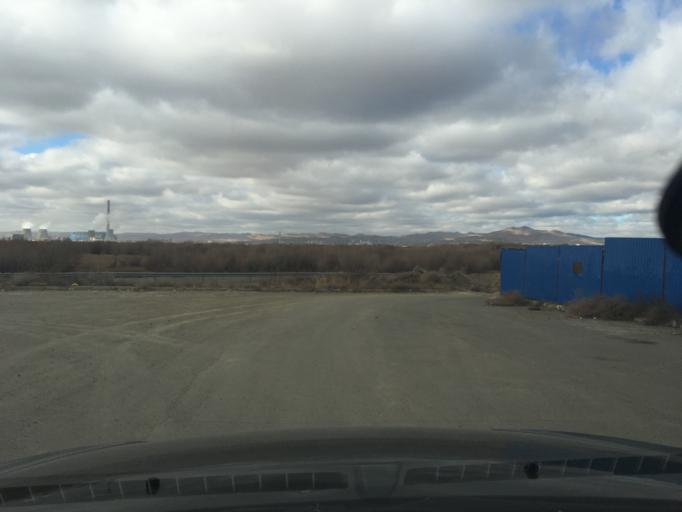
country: MN
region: Ulaanbaatar
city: Ulaanbaatar
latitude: 47.8804
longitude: 106.8488
